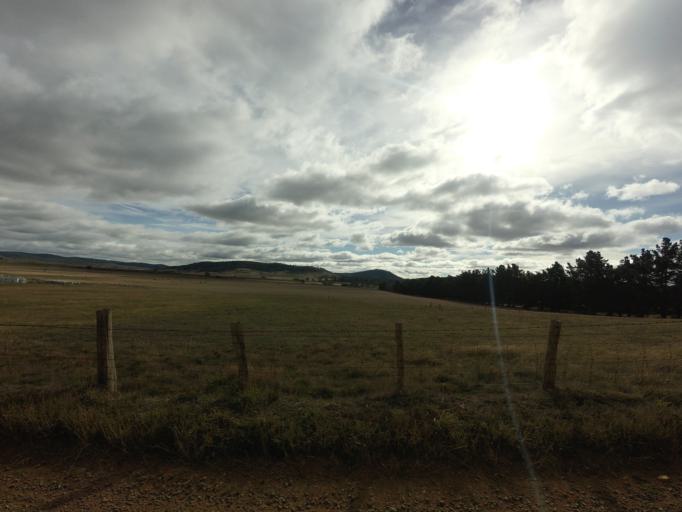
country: AU
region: Tasmania
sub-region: Brighton
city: Bridgewater
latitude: -42.4148
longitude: 147.3964
